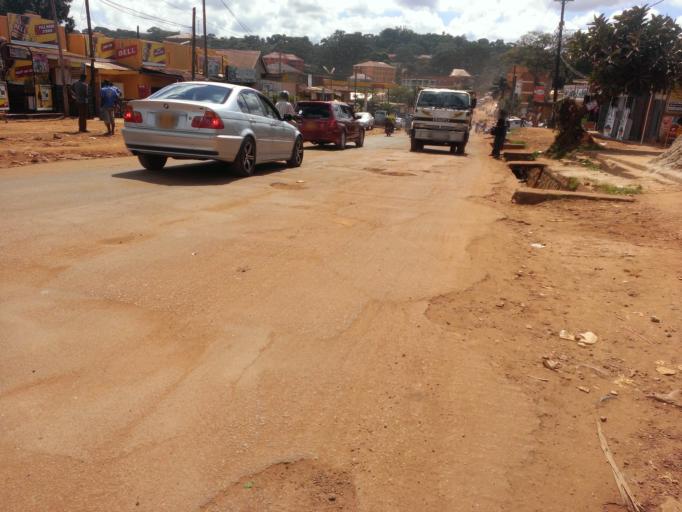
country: UG
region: Central Region
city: Kampala Central Division
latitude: 0.3262
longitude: 32.5625
